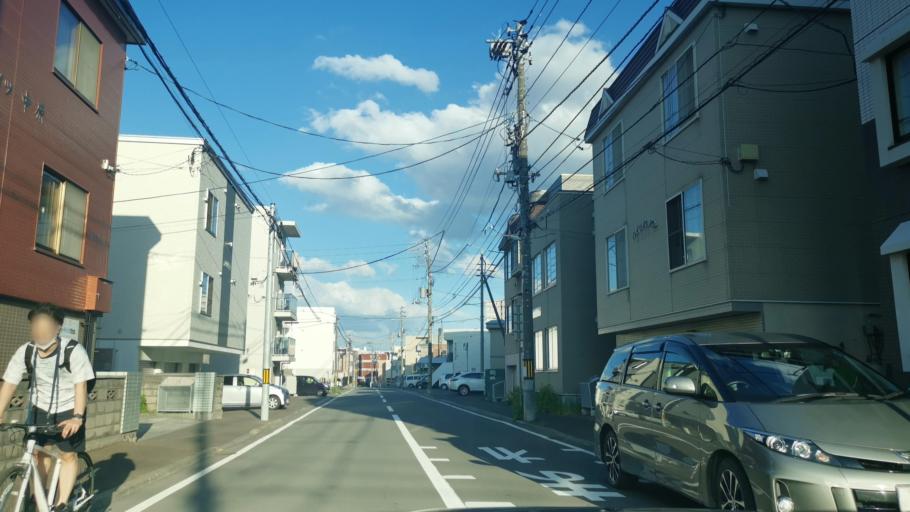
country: JP
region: Hokkaido
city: Sapporo
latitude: 43.0717
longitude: 141.3066
